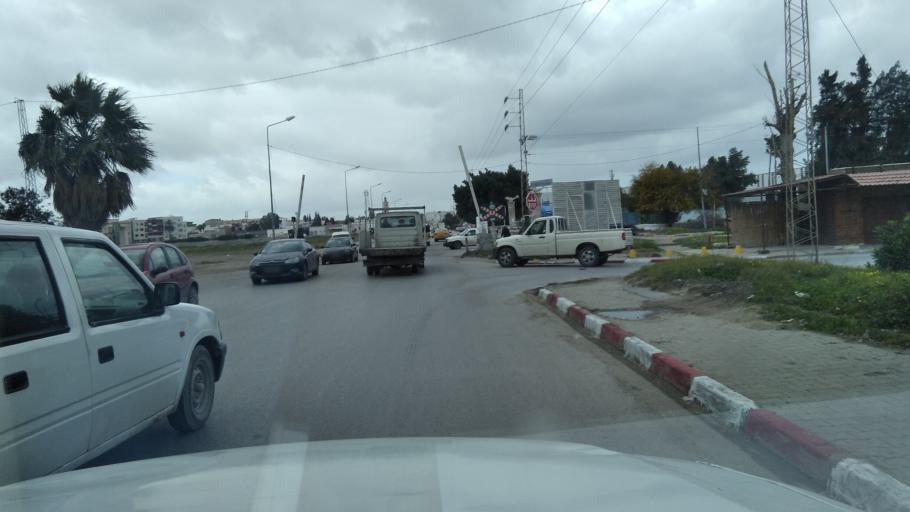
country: TN
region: Bin 'Arus
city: Ben Arous
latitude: 36.7482
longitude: 10.2294
